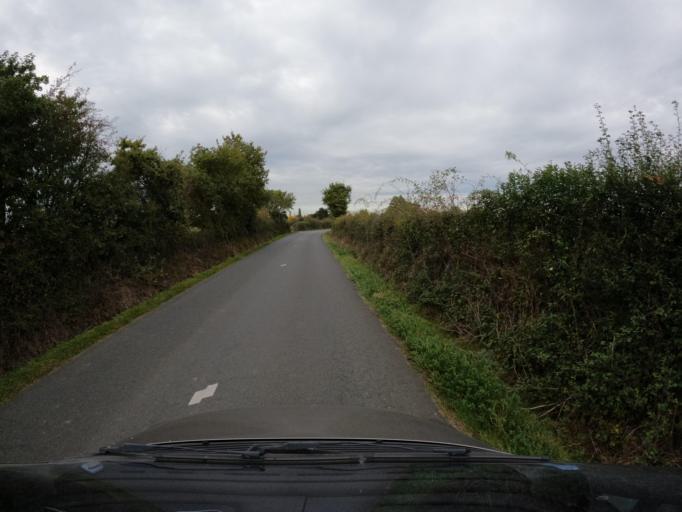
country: FR
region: Pays de la Loire
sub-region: Departement de Maine-et-Loire
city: La Seguiniere
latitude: 47.0491
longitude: -0.9389
